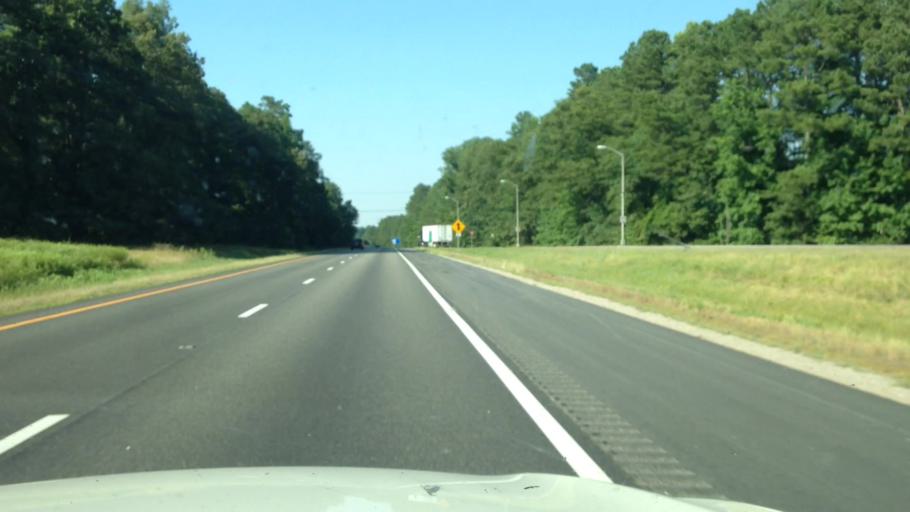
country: US
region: Virginia
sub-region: City of Petersburg
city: Petersburg
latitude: 37.0648
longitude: -77.3714
